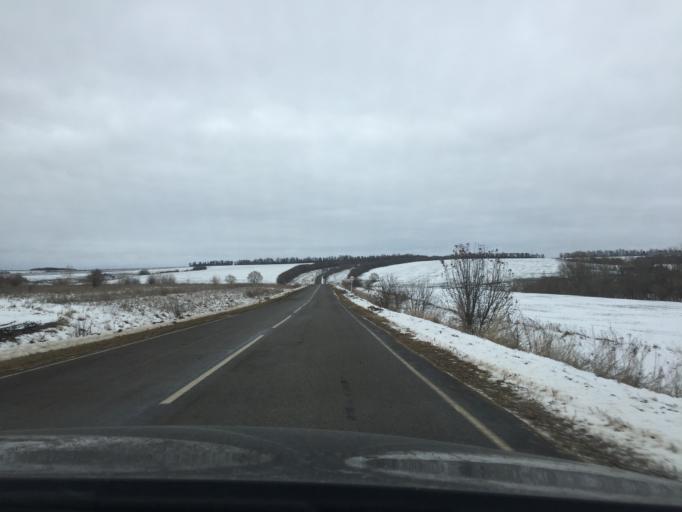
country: RU
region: Tula
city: Teploye
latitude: 53.8061
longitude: 37.5548
